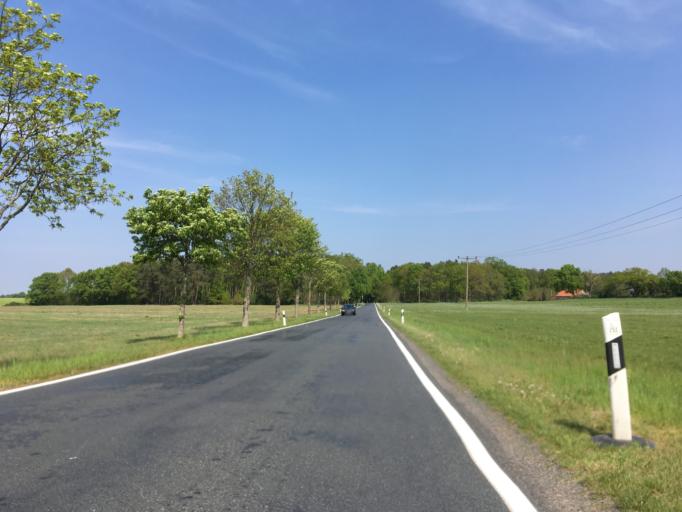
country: DE
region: Brandenburg
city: Melchow
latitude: 52.7211
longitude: 13.7128
